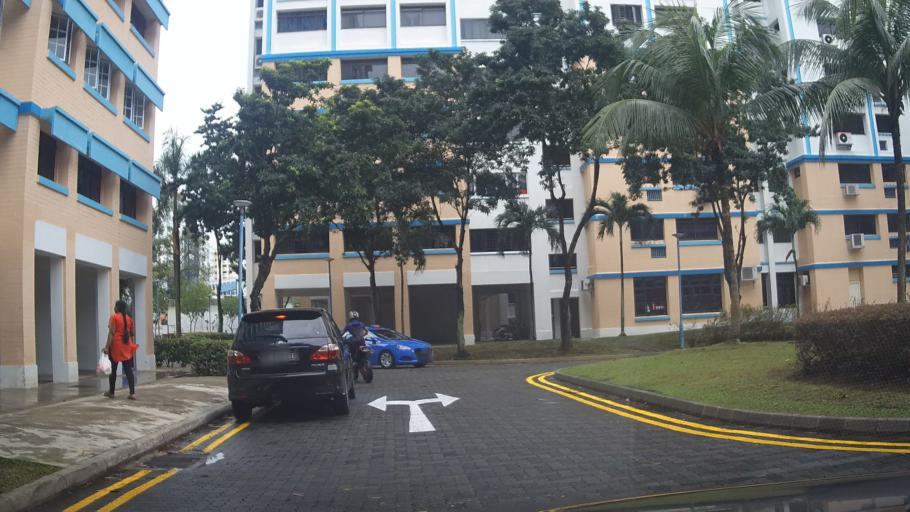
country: MY
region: Johor
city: Johor Bahru
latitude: 1.4478
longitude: 103.7990
